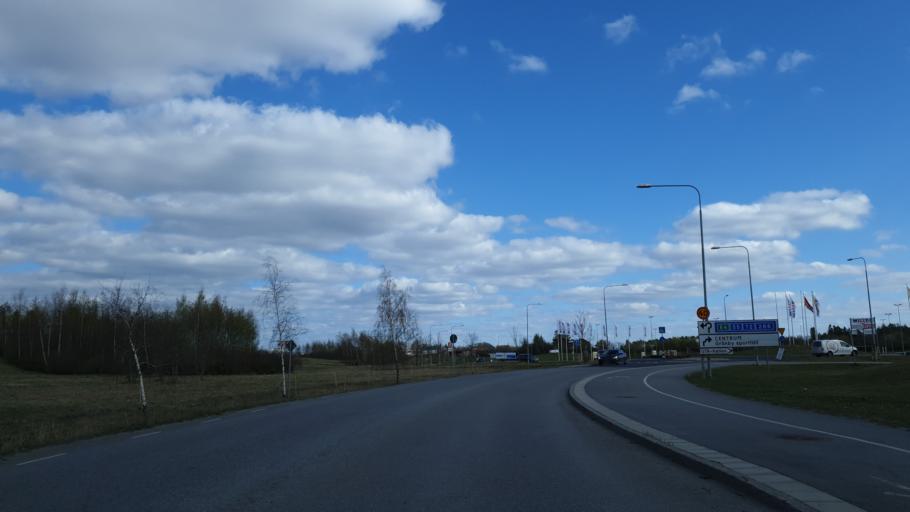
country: SE
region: Uppsala
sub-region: Uppsala Kommun
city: Gamla Uppsala
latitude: 59.8879
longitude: 17.6602
